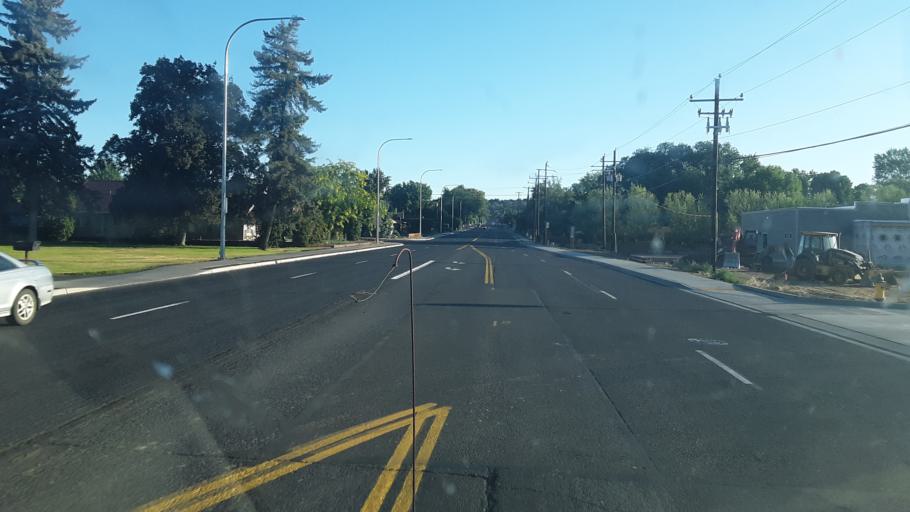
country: US
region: Washington
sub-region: Yakima County
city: West Valley
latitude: 46.5884
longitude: -120.6043
